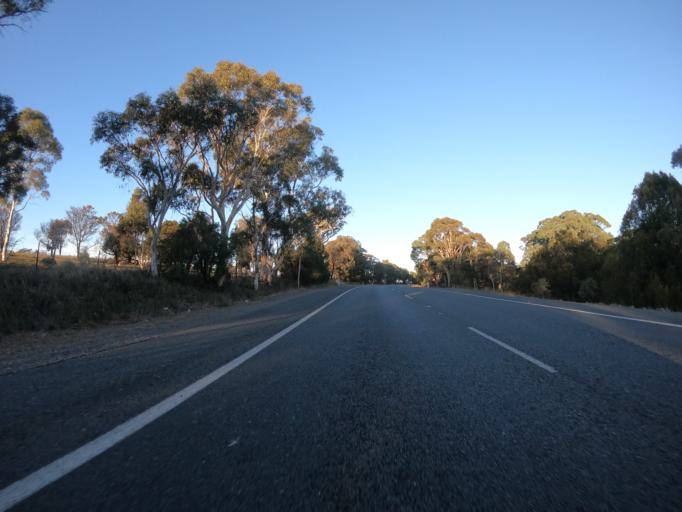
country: AU
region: New South Wales
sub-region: Goulburn Mulwaree
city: Goulburn
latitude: -34.8337
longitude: 149.5879
